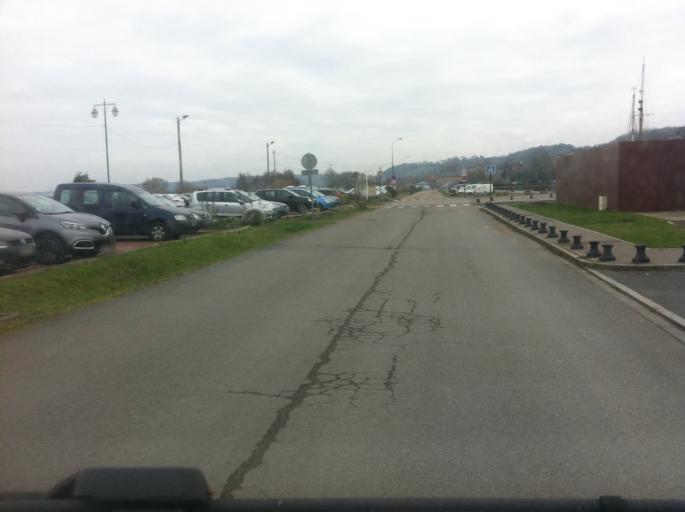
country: FR
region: Lower Normandy
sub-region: Departement du Calvados
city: Honfleur
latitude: 49.4212
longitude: 0.2371
